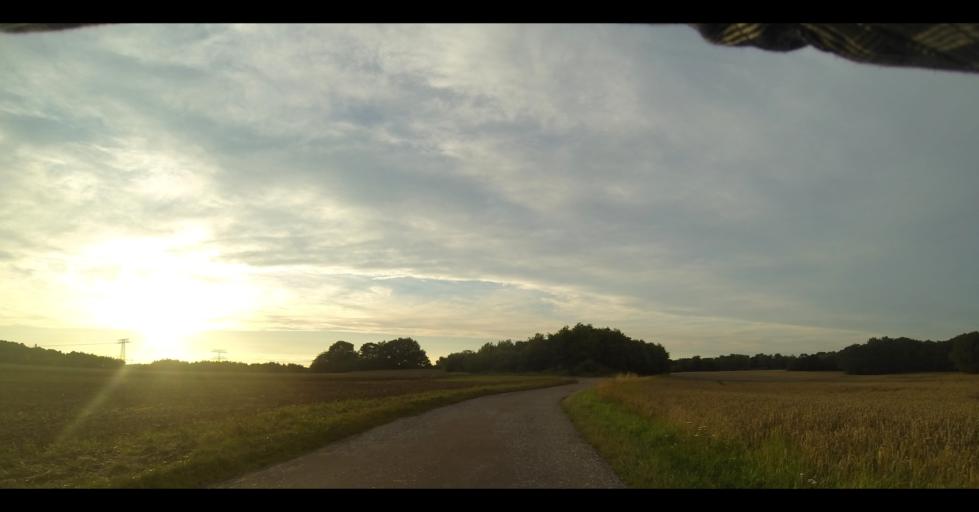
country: DE
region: Saxony
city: Moritzburg
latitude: 51.1341
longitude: 13.7213
